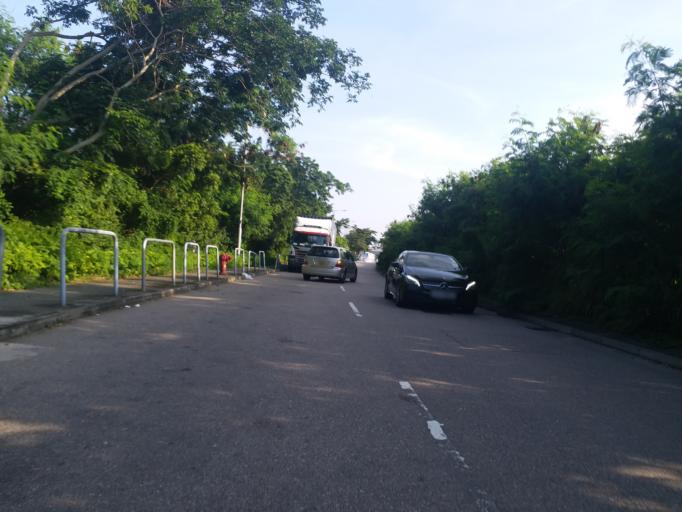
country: HK
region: Yuen Long
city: Yuen Long Kau Hui
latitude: 22.4748
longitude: 114.0516
